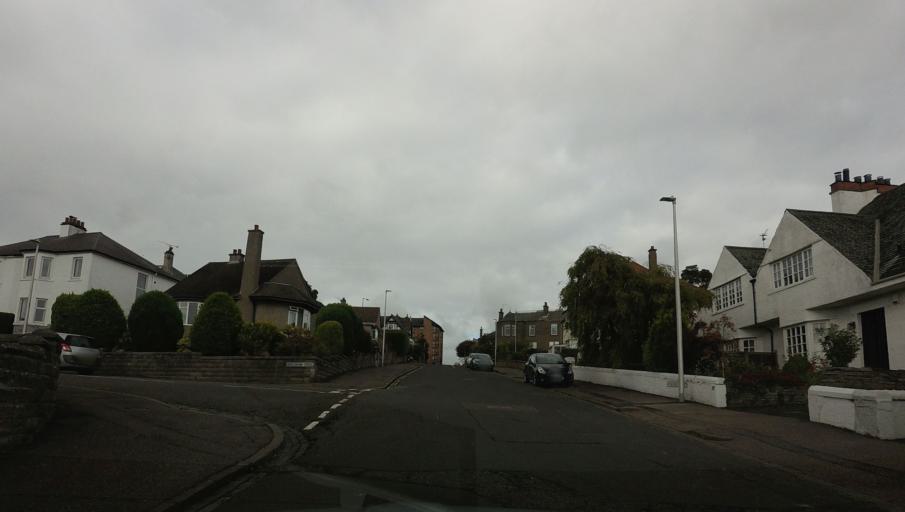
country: GB
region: Scotland
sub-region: Dundee City
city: Dundee
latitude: 56.4591
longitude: -3.0018
